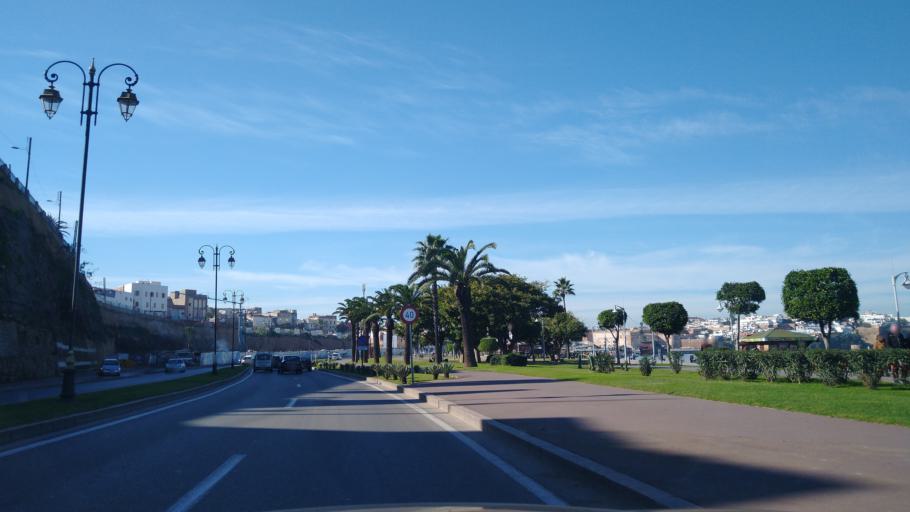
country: MA
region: Rabat-Sale-Zemmour-Zaer
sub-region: Rabat
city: Rabat
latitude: 34.0272
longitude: -6.8279
